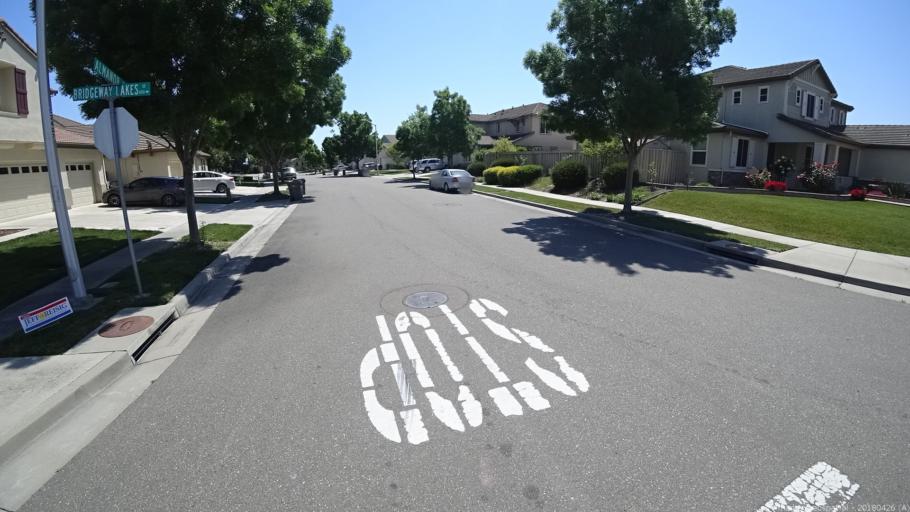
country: US
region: California
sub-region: Yolo County
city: West Sacramento
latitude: 38.5319
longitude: -121.5749
